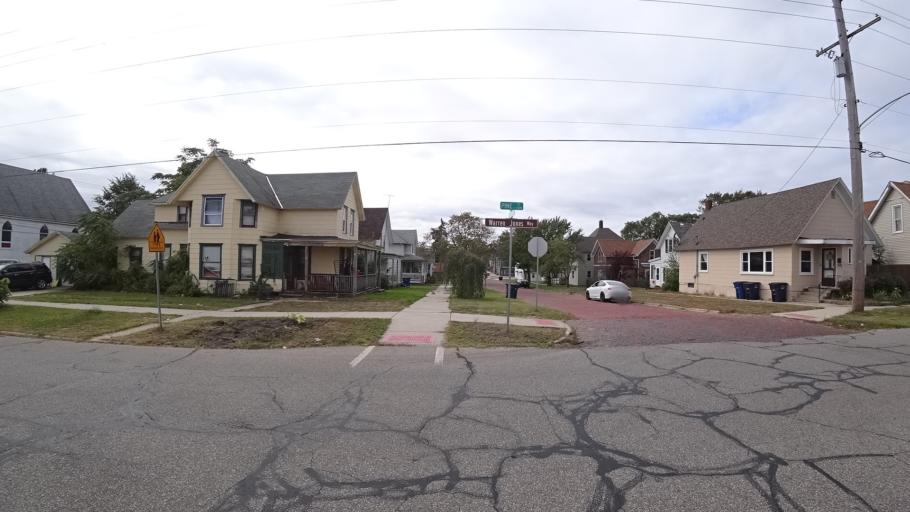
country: US
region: Indiana
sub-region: LaPorte County
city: Michigan City
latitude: 41.7096
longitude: -86.8963
